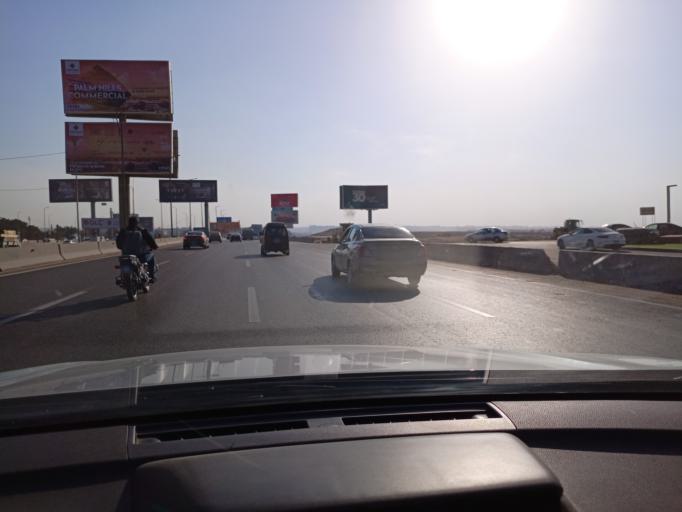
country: EG
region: Muhafazat al Qalyubiyah
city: Al Khankah
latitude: 30.0722
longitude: 31.4295
